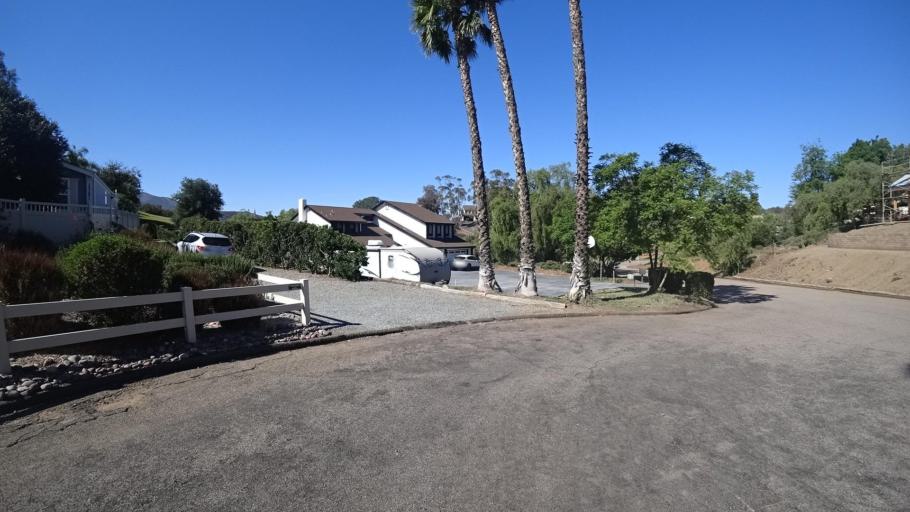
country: US
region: California
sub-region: San Diego County
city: Jamul
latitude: 32.7303
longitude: -116.9028
